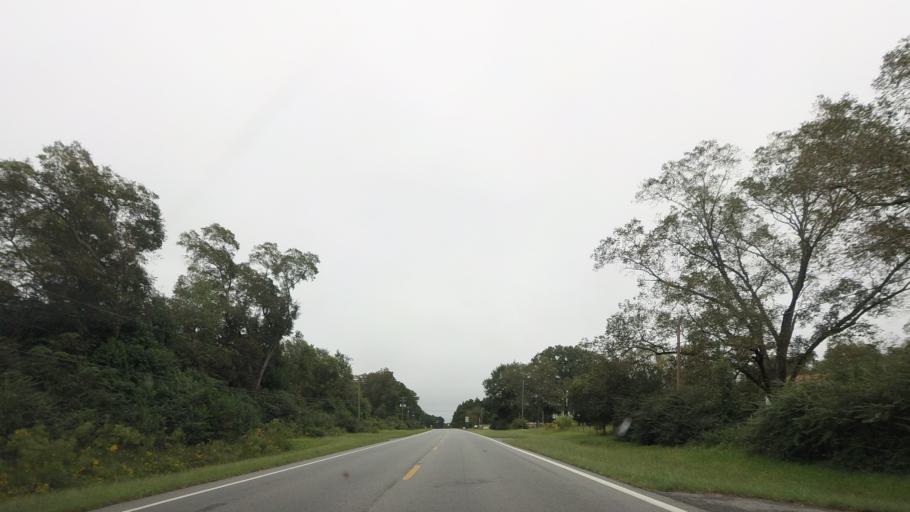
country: US
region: Georgia
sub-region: Berrien County
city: Nashville
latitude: 31.2298
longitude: -83.2469
